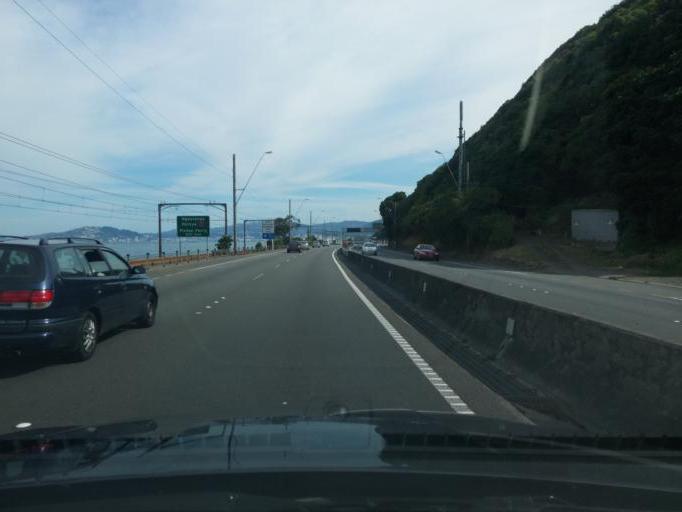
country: NZ
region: Wellington
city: Petone
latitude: -41.2346
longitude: 174.8348
